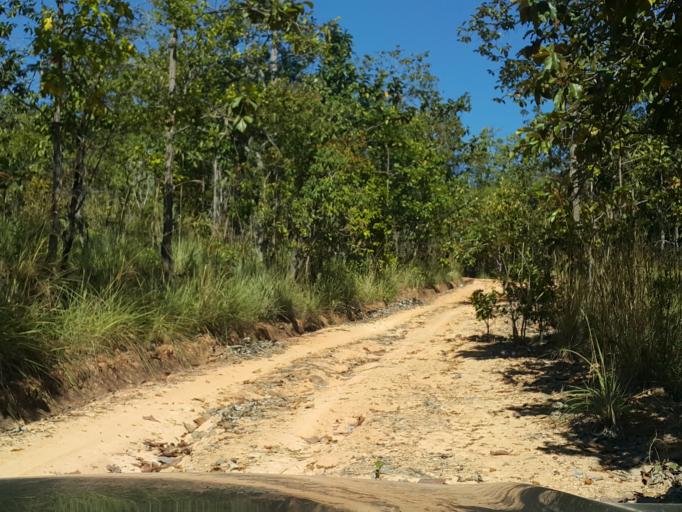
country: TH
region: Chiang Mai
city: Hang Dong
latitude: 18.7886
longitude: 98.8664
